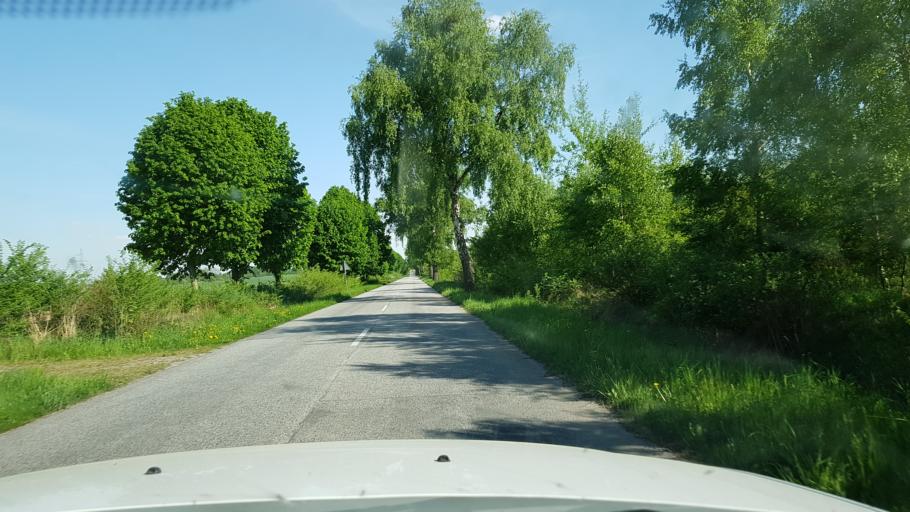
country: PL
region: West Pomeranian Voivodeship
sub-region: Powiat lobeski
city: Resko
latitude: 53.8160
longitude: 15.3989
